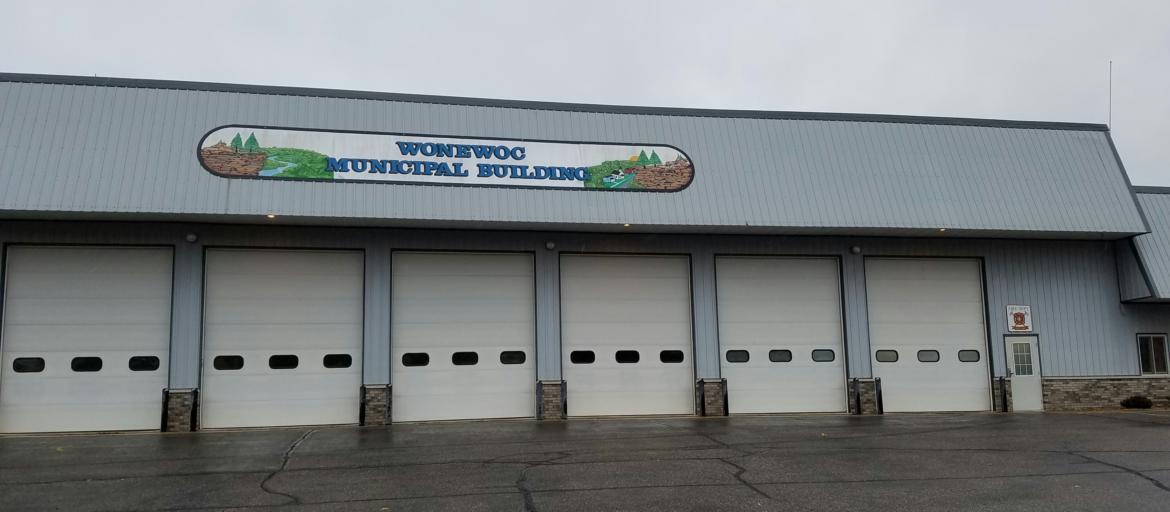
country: US
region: Wisconsin
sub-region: Juneau County
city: Elroy
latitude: 43.6536
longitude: -90.2244
